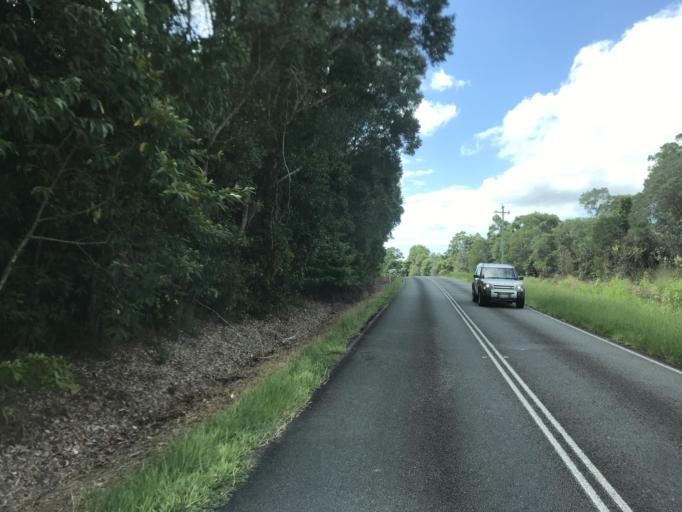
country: AU
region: Queensland
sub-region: Cassowary Coast
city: Innisfail
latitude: -17.8390
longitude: 146.0529
